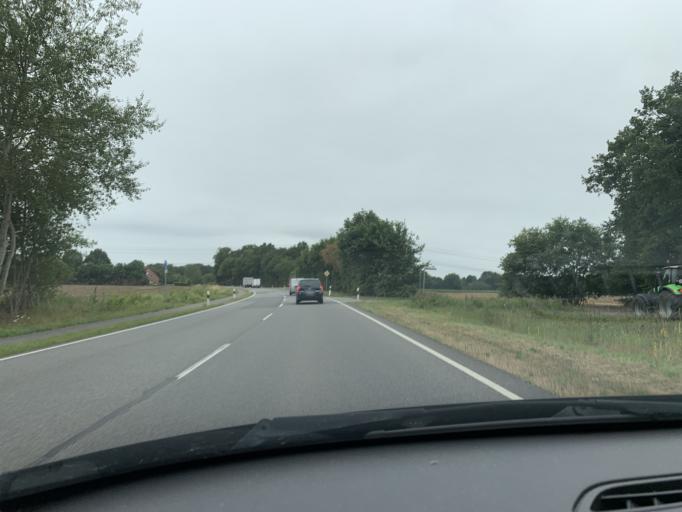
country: DE
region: Lower Saxony
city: Bawinkel
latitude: 52.5787
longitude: 7.3776
